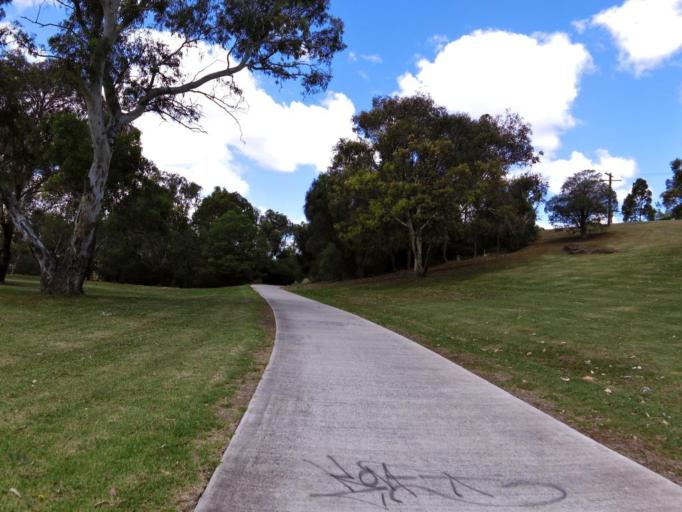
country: AU
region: Victoria
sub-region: Hume
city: Westmeadows
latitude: -37.6791
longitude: 144.8906
